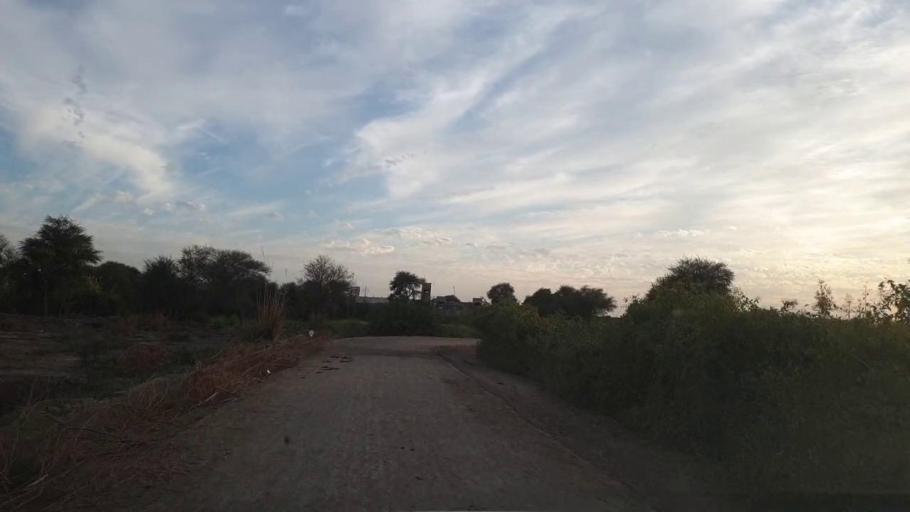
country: PK
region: Sindh
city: Pithoro
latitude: 25.6033
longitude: 69.2067
